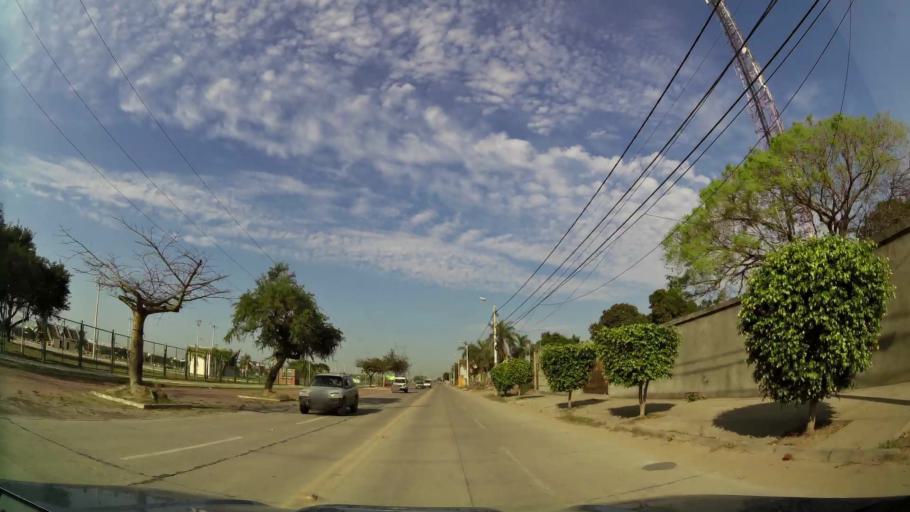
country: BO
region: Santa Cruz
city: Santa Cruz de la Sierra
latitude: -17.7387
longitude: -63.1441
